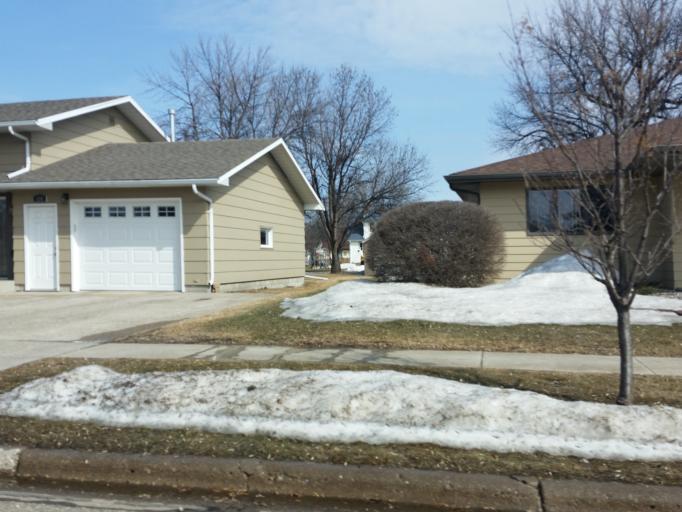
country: US
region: North Dakota
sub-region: Walsh County
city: Grafton
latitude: 48.4188
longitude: -97.4040
